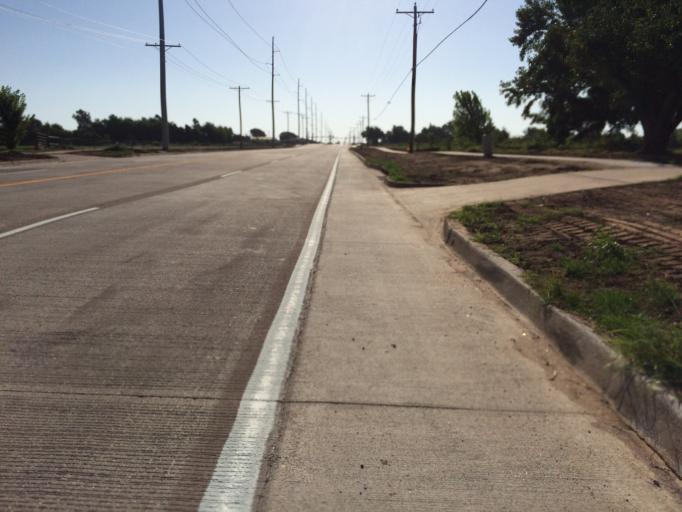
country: US
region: Oklahoma
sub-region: Cleveland County
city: Noble
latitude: 35.1751
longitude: -97.4183
